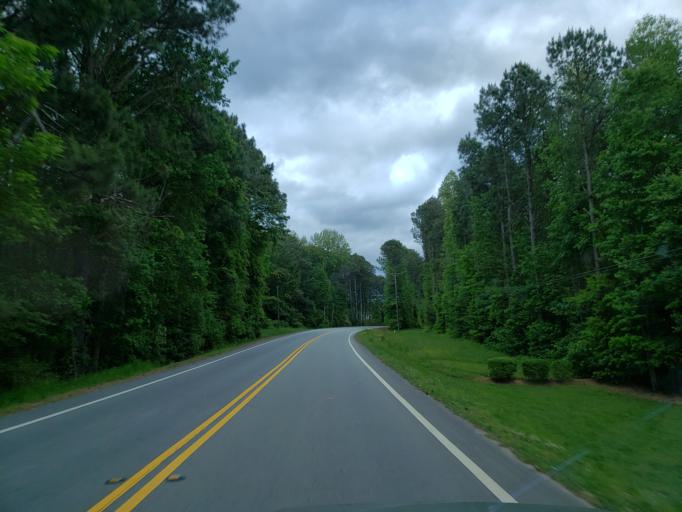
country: US
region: Georgia
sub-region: Paulding County
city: Dallas
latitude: 33.8718
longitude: -84.8684
